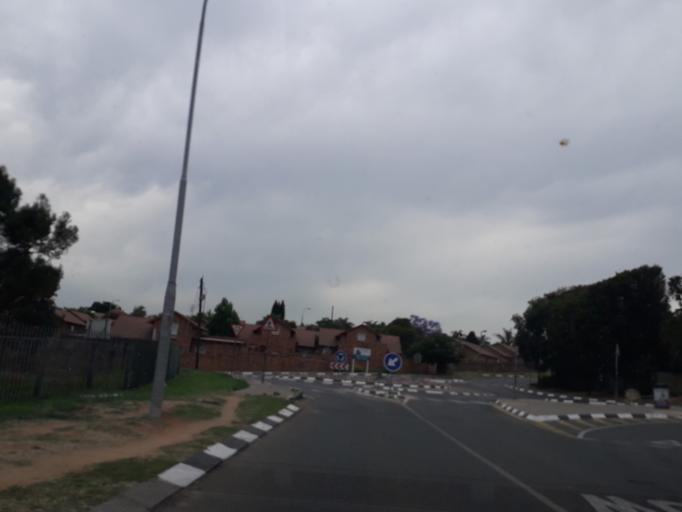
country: ZA
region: Gauteng
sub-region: City of Johannesburg Metropolitan Municipality
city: Roodepoort
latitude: -26.1107
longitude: 27.9163
